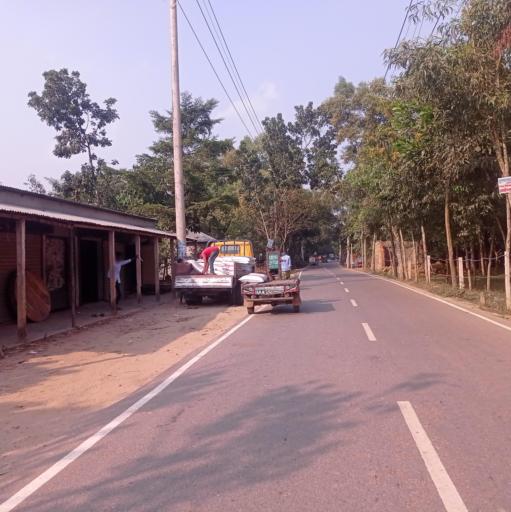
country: BD
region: Dhaka
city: Bhairab Bazar
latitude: 24.0659
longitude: 90.8415
